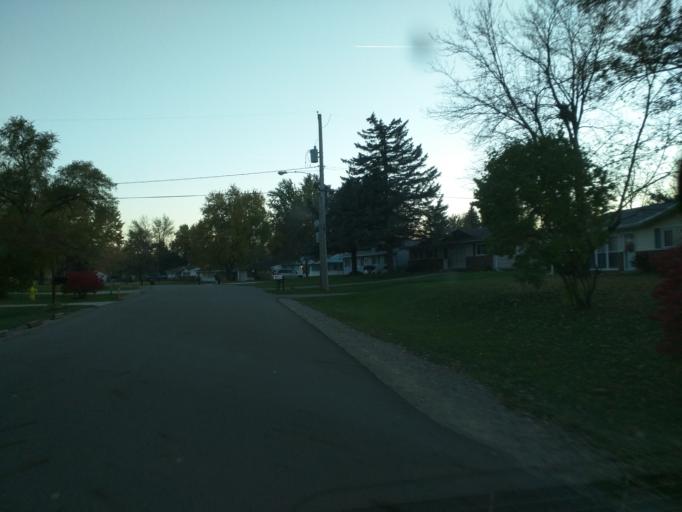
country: US
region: Michigan
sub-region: Eaton County
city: Waverly
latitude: 42.7384
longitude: -84.6071
